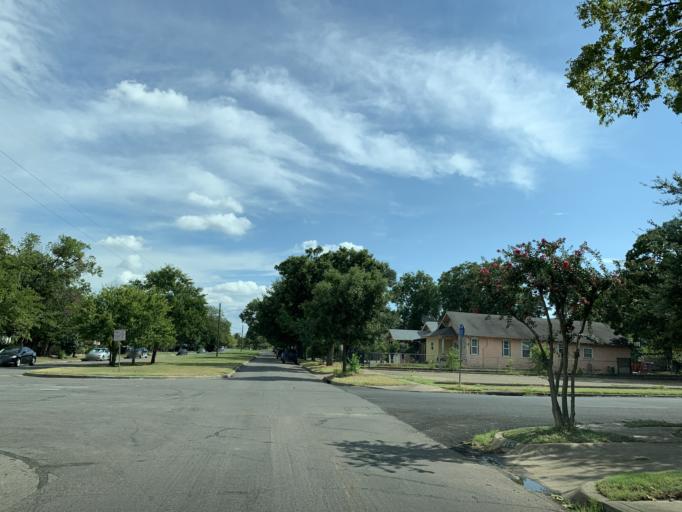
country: US
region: Texas
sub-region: Dallas County
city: Cockrell Hill
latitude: 32.7396
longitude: -96.8529
